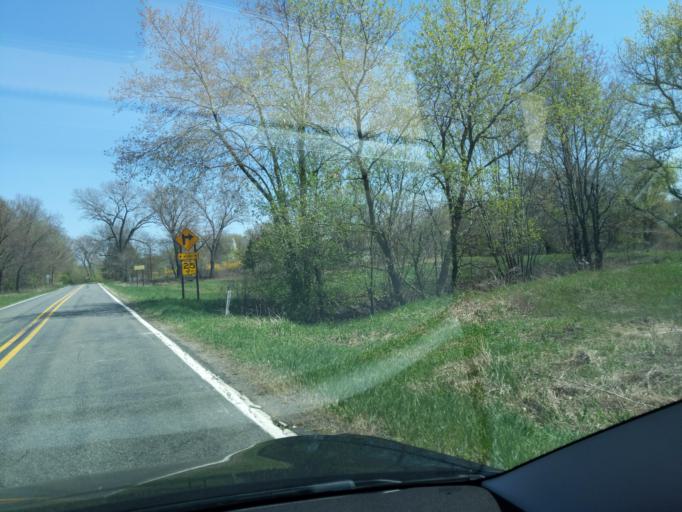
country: US
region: Michigan
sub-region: Ingham County
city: Stockbridge
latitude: 42.4925
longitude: -84.2215
